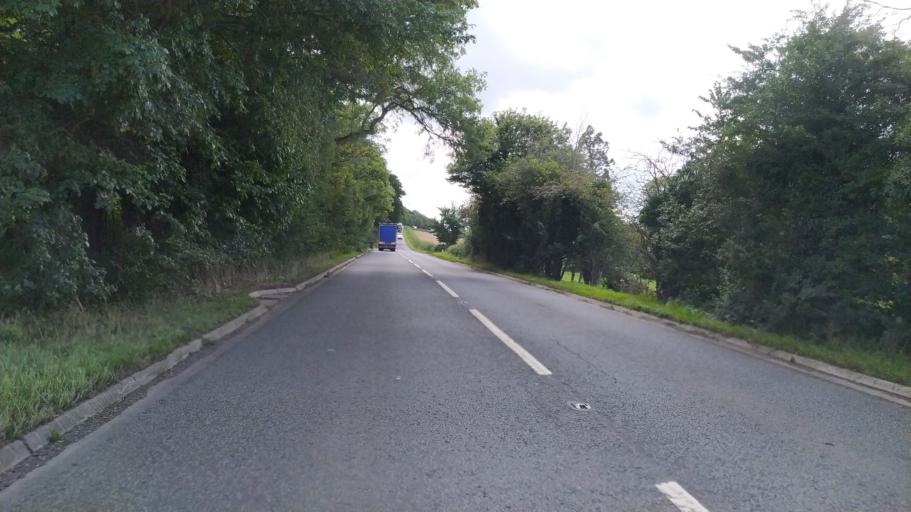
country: GB
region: England
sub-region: Wiltshire
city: North Bradley
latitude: 51.3093
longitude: -2.1718
